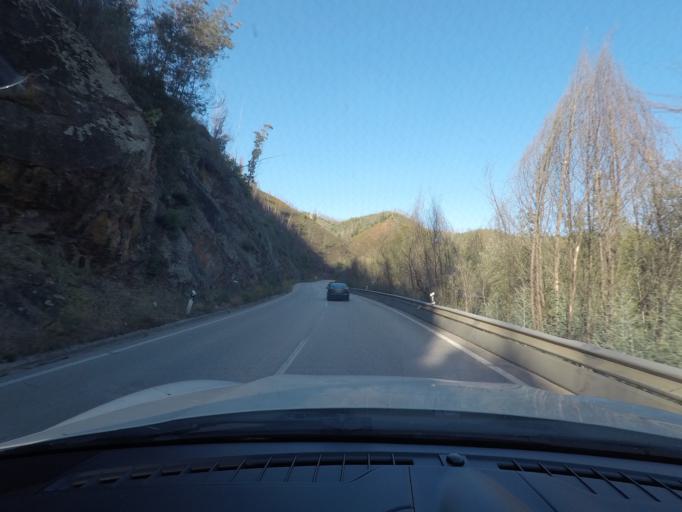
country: PT
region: Coimbra
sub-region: Vila Nova de Poiares
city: Poiares
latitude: 40.1738
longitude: -8.3081
